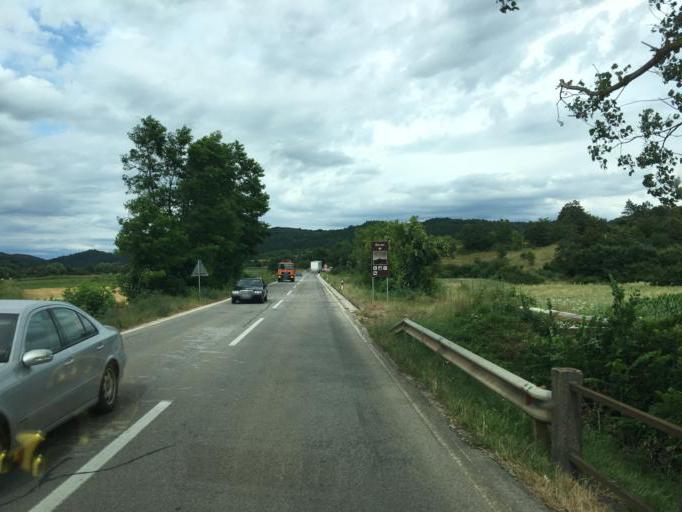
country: HR
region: Istarska
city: Pazin
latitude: 45.2532
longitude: 13.8892
